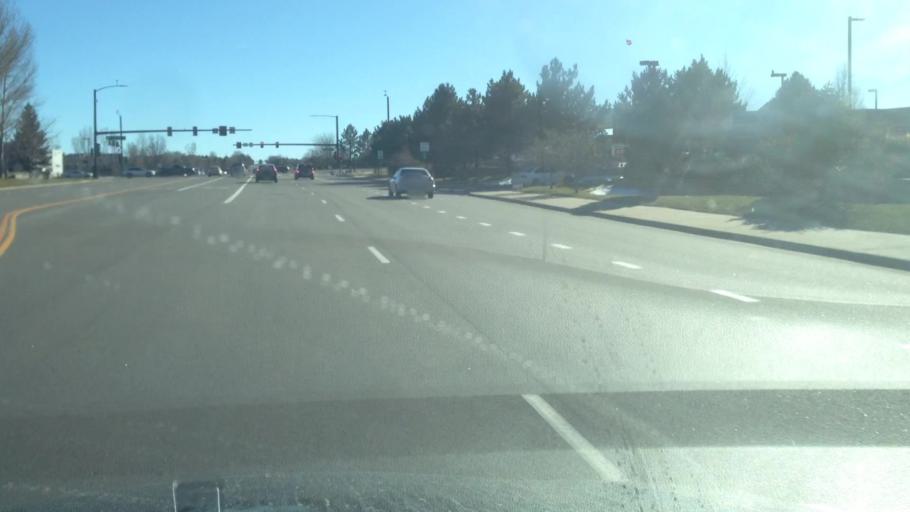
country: US
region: Colorado
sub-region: Douglas County
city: Stonegate
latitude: 39.5354
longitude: -104.7935
